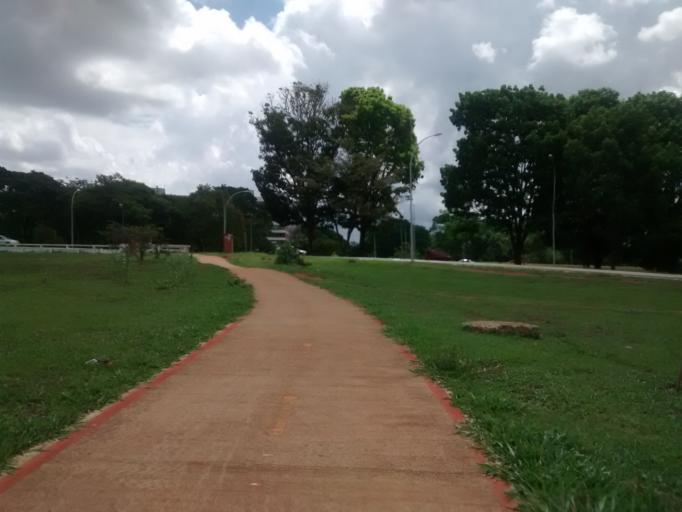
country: BR
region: Federal District
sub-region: Brasilia
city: Brasilia
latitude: -15.7644
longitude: -47.8818
